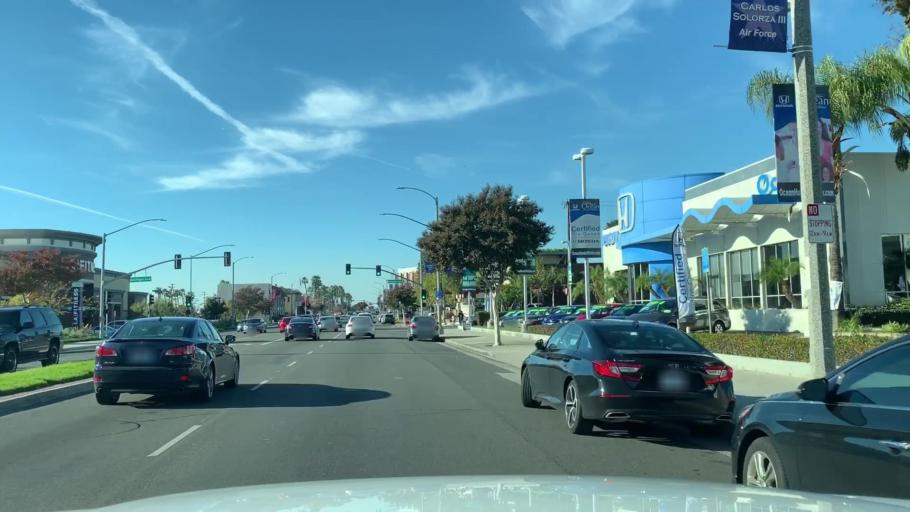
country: US
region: California
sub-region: Los Angeles County
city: South Whittier
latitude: 33.9593
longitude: -118.0259
